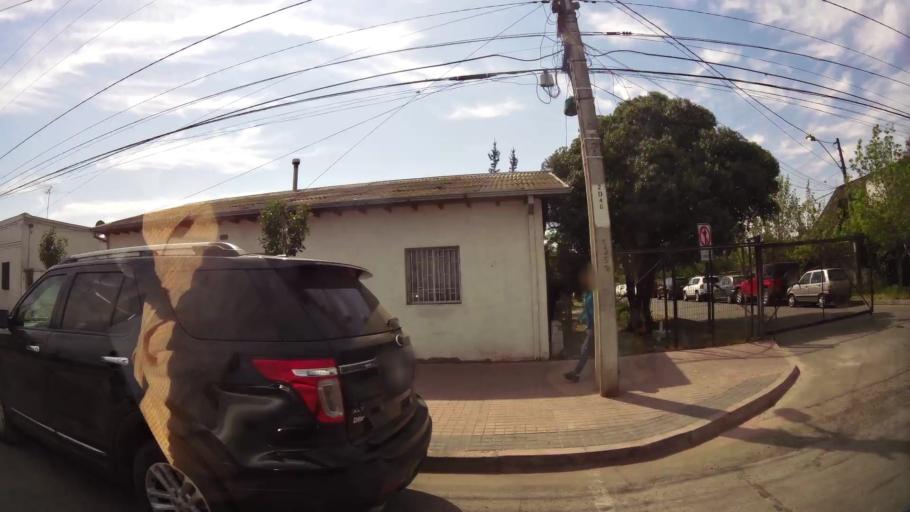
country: CL
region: Santiago Metropolitan
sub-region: Provincia de Talagante
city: Talagante
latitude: -33.6614
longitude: -70.9287
